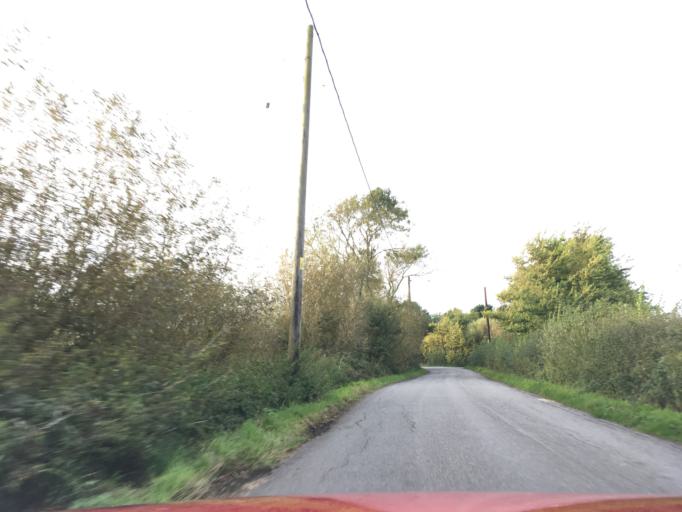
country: GB
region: England
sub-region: South Gloucestershire
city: Severn Beach
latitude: 51.5760
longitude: -2.6355
